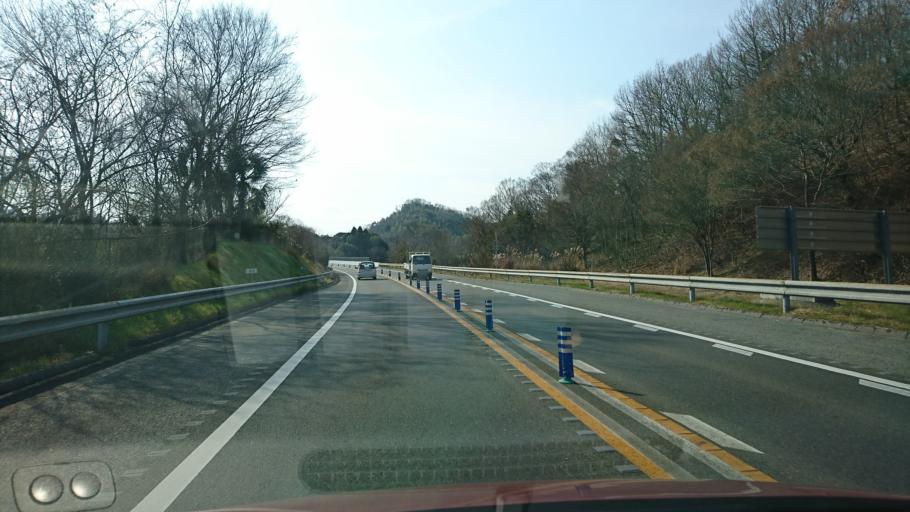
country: JP
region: Hiroshima
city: Onomichi
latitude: 34.3939
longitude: 133.2068
